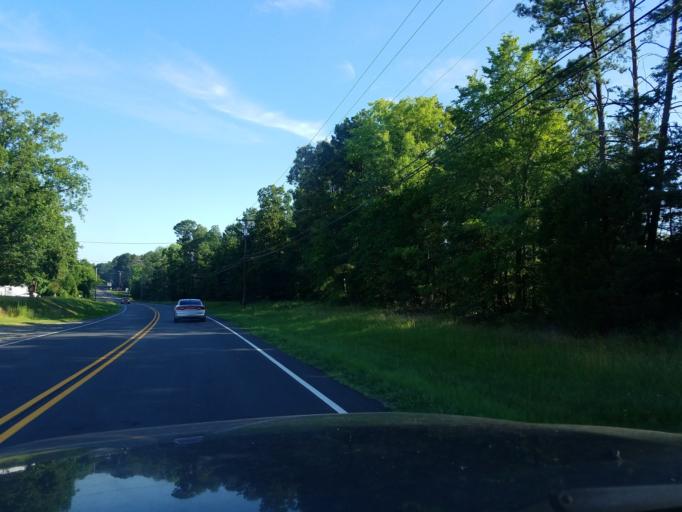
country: US
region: North Carolina
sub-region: Granville County
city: Butner
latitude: 36.1266
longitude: -78.7515
